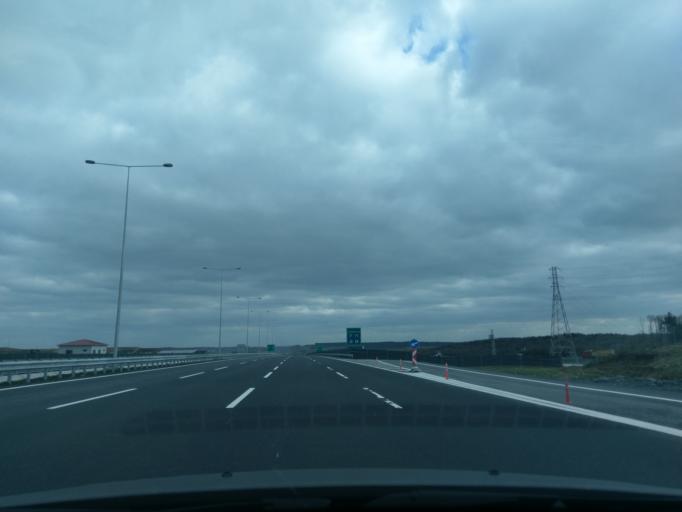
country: TR
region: Istanbul
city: Durusu
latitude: 41.2446
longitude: 28.6966
